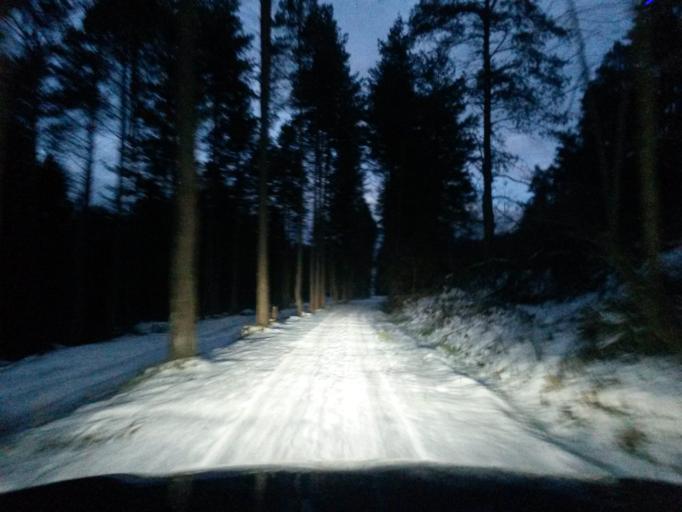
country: SK
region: Kosicky
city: Medzev
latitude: 48.7911
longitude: 20.8060
